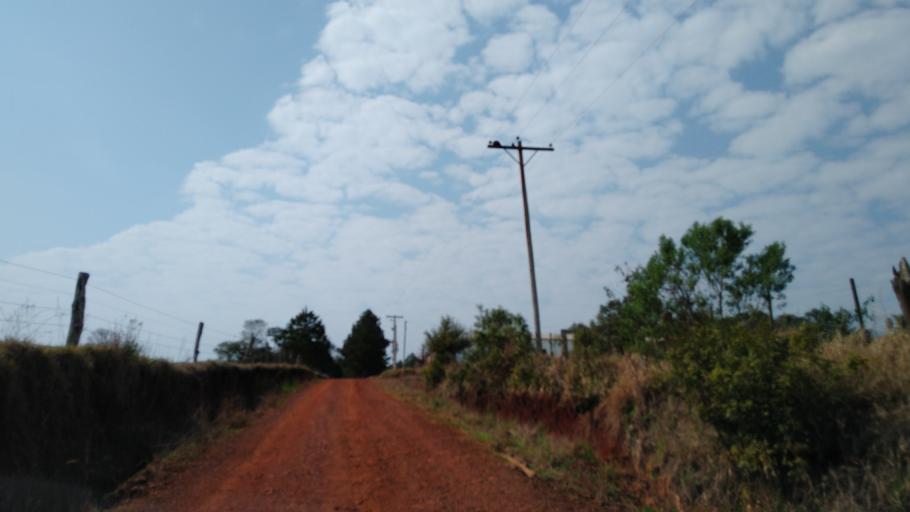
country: AR
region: Misiones
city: Capiovi
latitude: -26.9528
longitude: -55.0493
